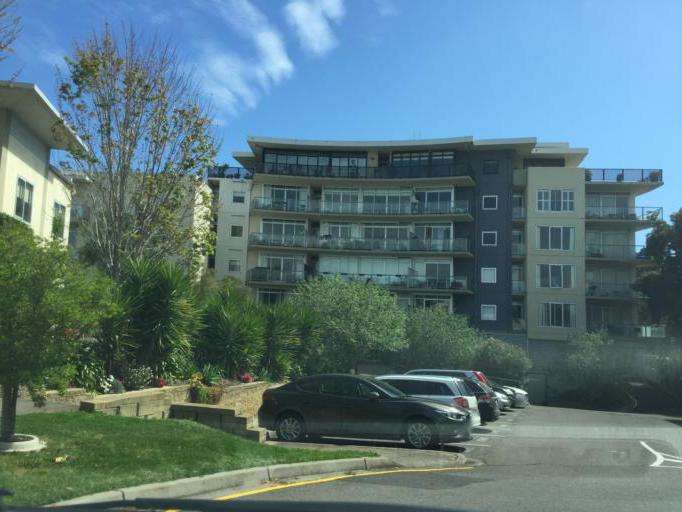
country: AU
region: Victoria
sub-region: Maribyrnong
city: Maribyrnong
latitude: -37.7758
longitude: 144.8924
